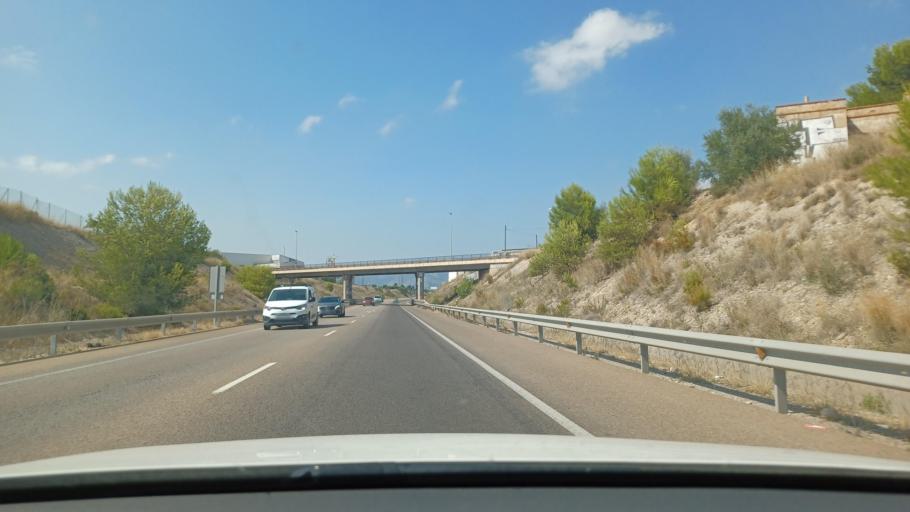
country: ES
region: Valencia
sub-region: Provincia de Castello
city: Vila-real
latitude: 39.9568
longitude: -0.0857
